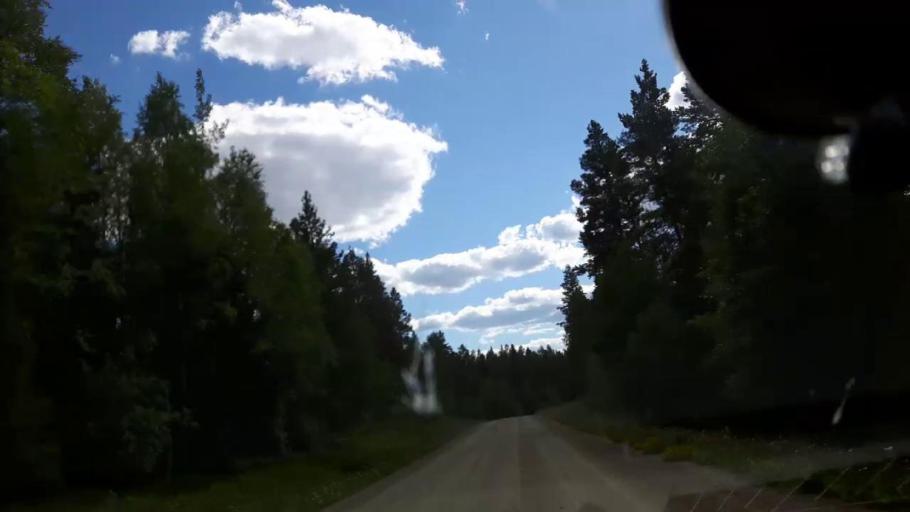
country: SE
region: Vaesternorrland
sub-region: Ange Kommun
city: Ange
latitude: 62.7299
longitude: 15.6442
